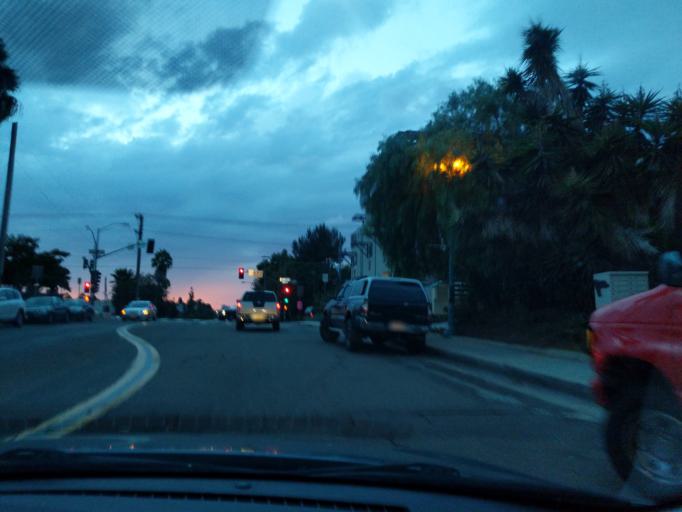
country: US
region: California
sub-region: San Diego County
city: San Diego
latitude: 32.7159
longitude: -117.1289
